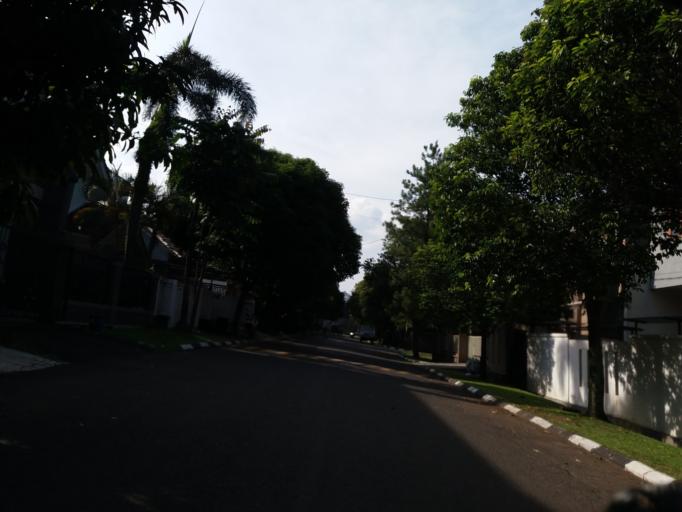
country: ID
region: West Java
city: Bandung
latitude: -6.9607
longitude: 107.6306
